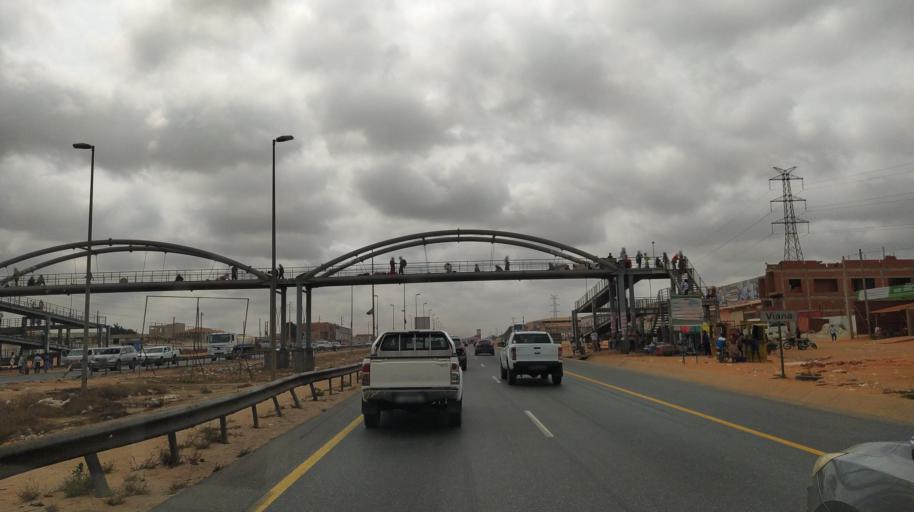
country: AO
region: Luanda
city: Luanda
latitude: -8.9730
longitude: 13.3054
